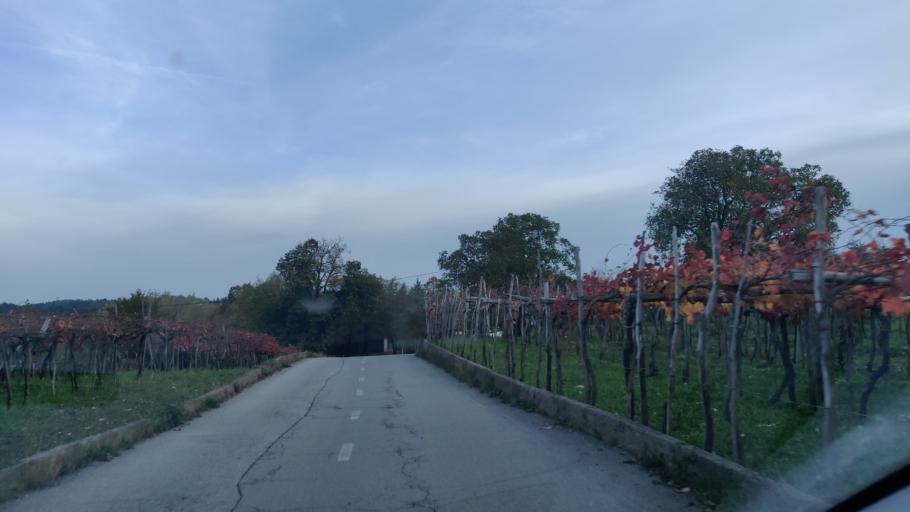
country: SI
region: Sezana
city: Sezana
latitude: 45.7869
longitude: 13.8634
